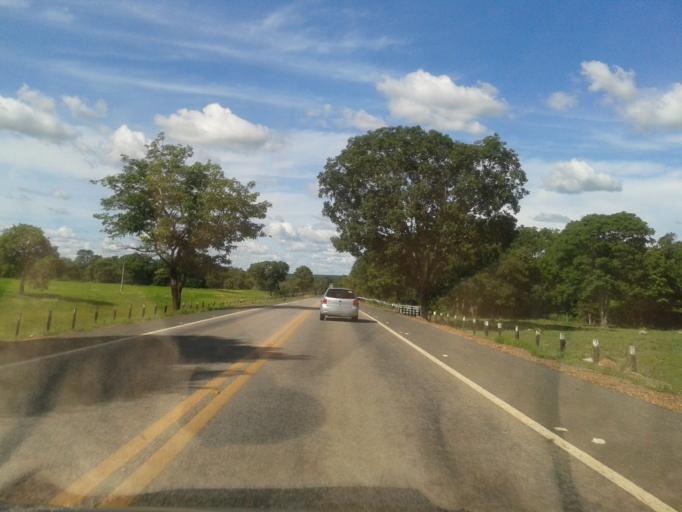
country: BR
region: Goias
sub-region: Mozarlandia
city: Mozarlandia
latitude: -15.0064
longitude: -50.5914
